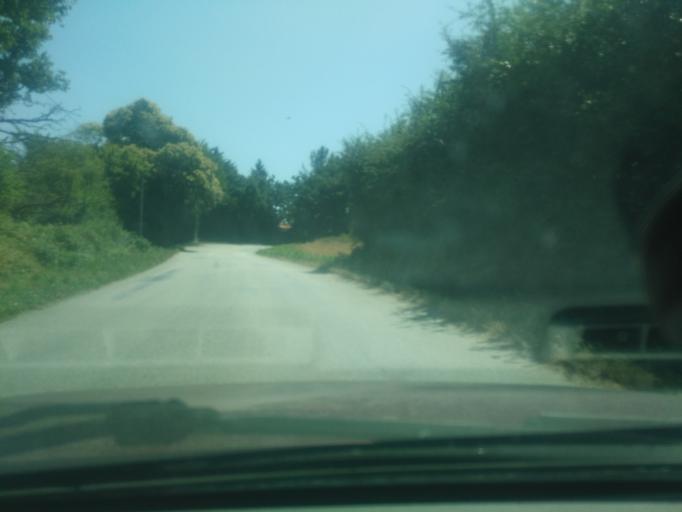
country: FR
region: Pays de la Loire
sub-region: Departement de la Vendee
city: Dompierre-sur-Yon
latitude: 46.7173
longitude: -1.3962
